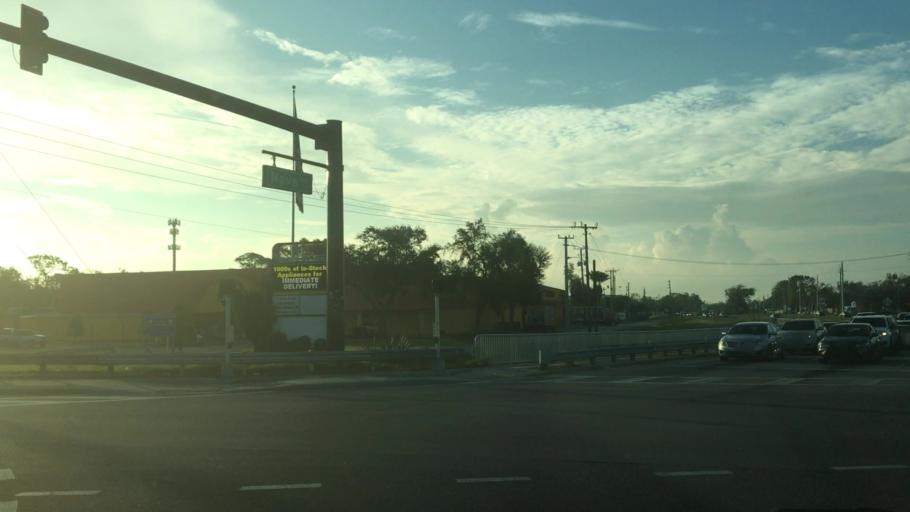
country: US
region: Florida
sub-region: Volusia County
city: South Daytona
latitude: 29.1754
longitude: -81.0285
